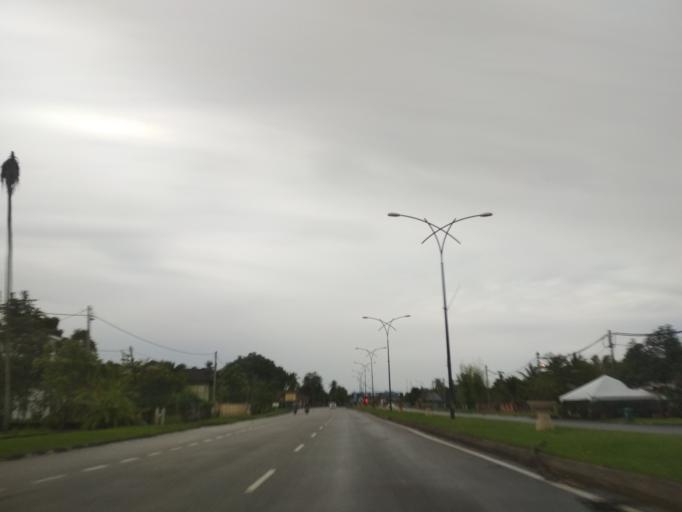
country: MY
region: Perlis
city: Kangar
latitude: 6.4624
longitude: 100.2088
